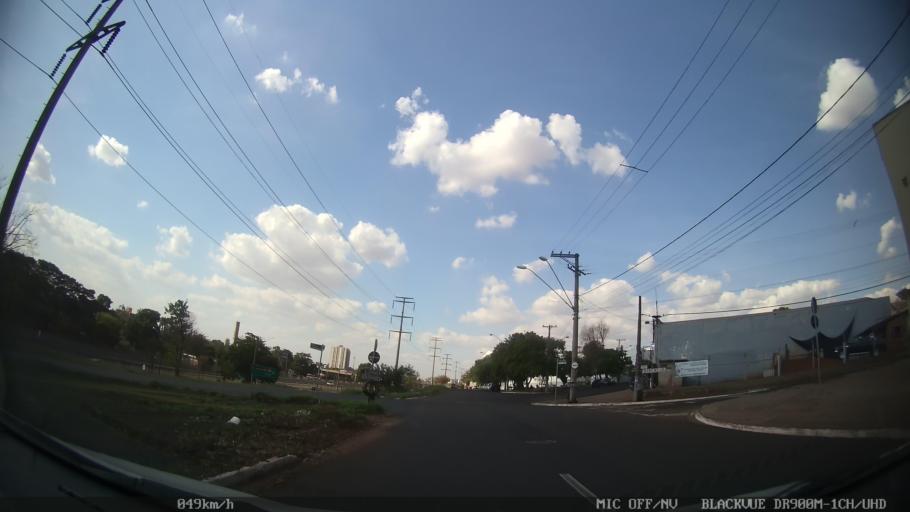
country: BR
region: Sao Paulo
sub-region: Ribeirao Preto
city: Ribeirao Preto
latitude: -21.1797
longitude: -47.8382
